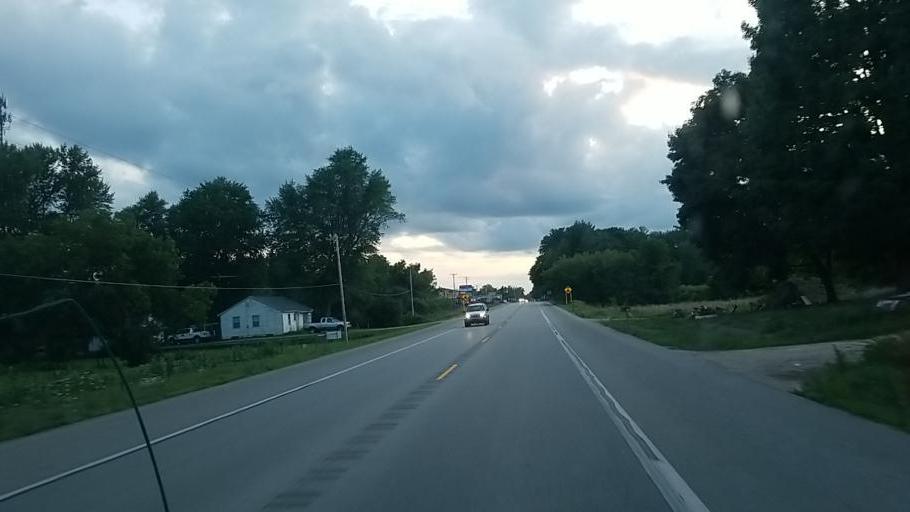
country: US
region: Michigan
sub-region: Newaygo County
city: Fremont
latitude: 43.4674
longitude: -86.0332
